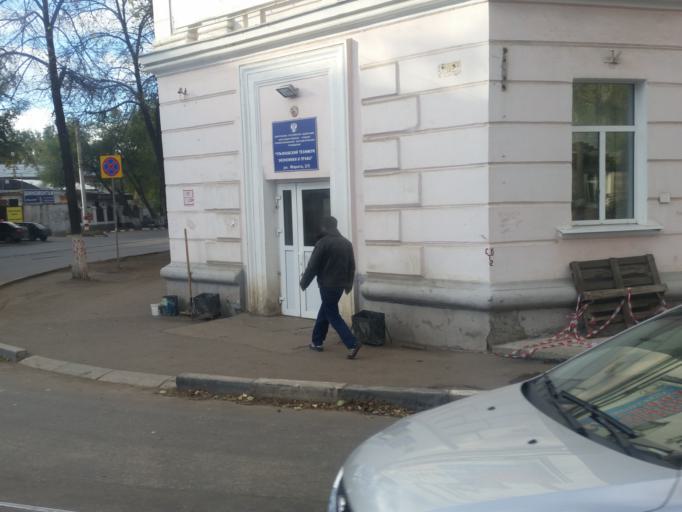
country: RU
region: Ulyanovsk
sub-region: Ulyanovskiy Rayon
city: Ulyanovsk
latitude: 54.3240
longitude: 48.3936
